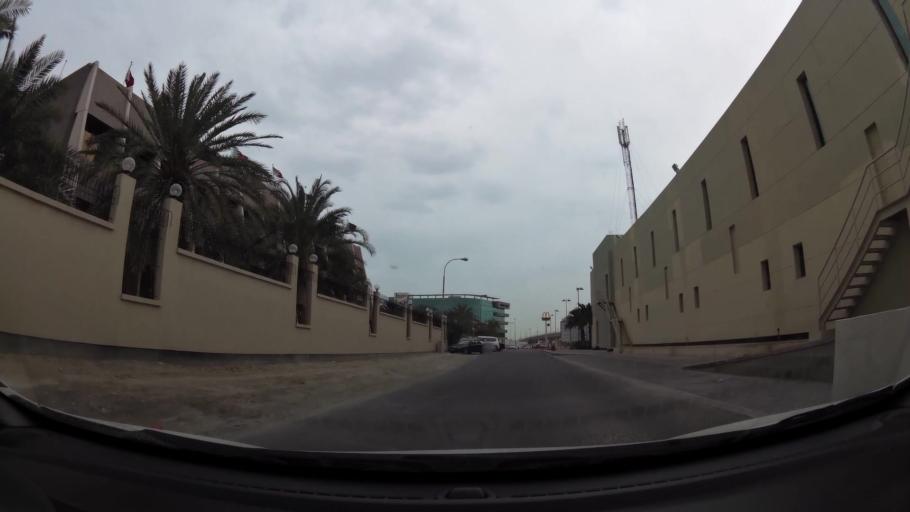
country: BH
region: Northern
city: Madinat `Isa
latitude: 26.1674
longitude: 50.5416
